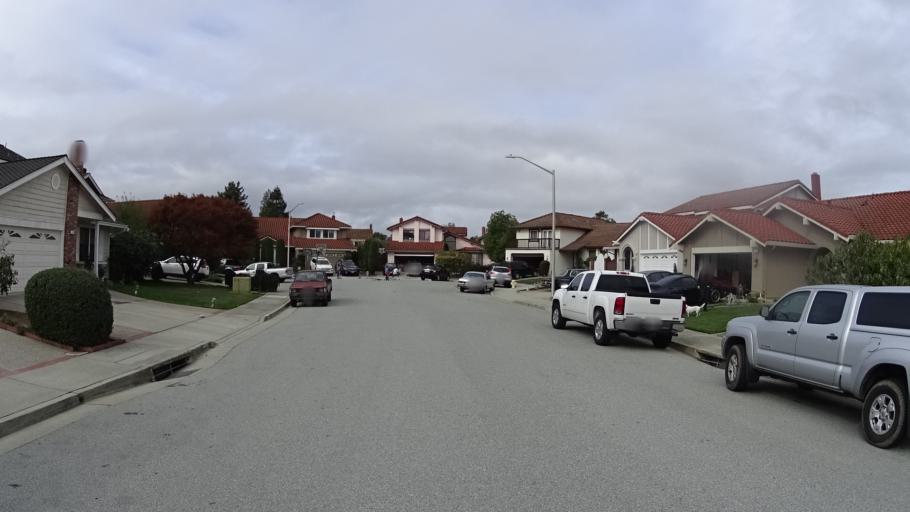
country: US
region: California
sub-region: San Mateo County
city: Belmont
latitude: 37.5317
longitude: -122.2797
